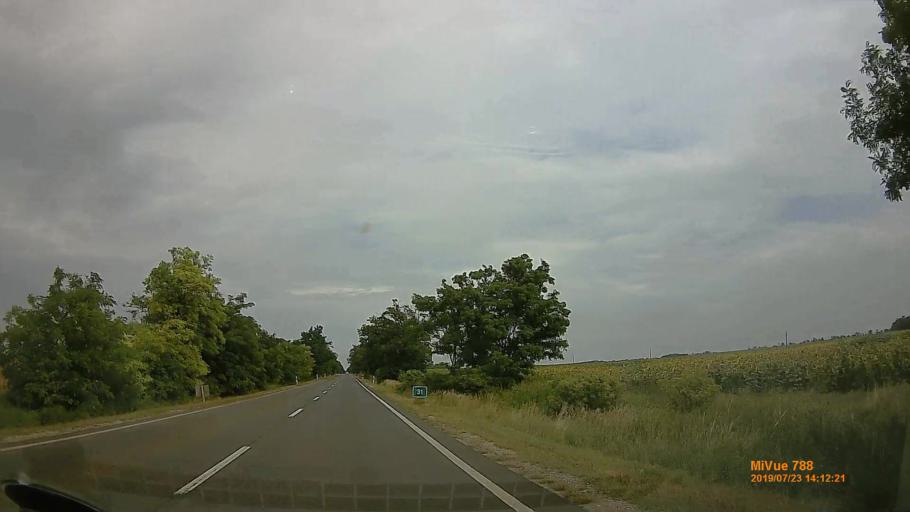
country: HU
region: Szabolcs-Szatmar-Bereg
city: Nagycserkesz
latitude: 47.9591
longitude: 21.4520
